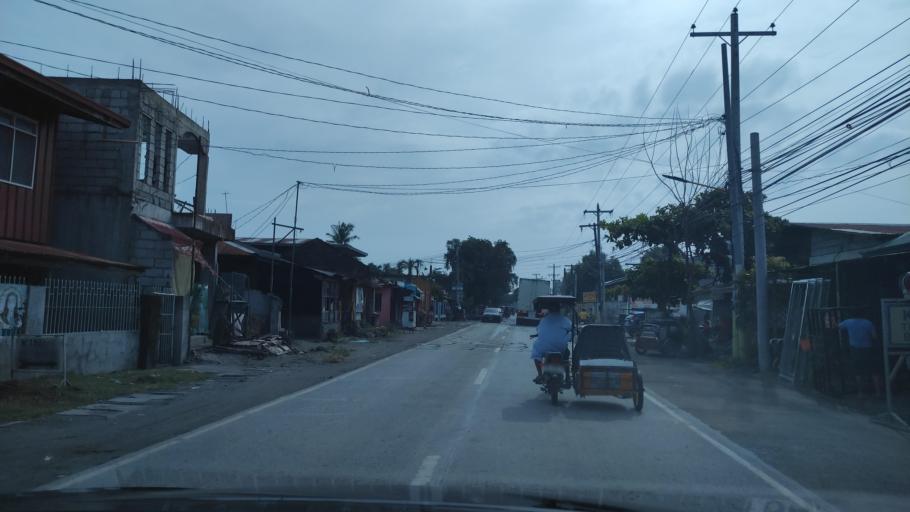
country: PH
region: Central Luzon
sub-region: Province of Nueva Ecija
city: Cabiao
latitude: 15.2421
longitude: 120.8518
